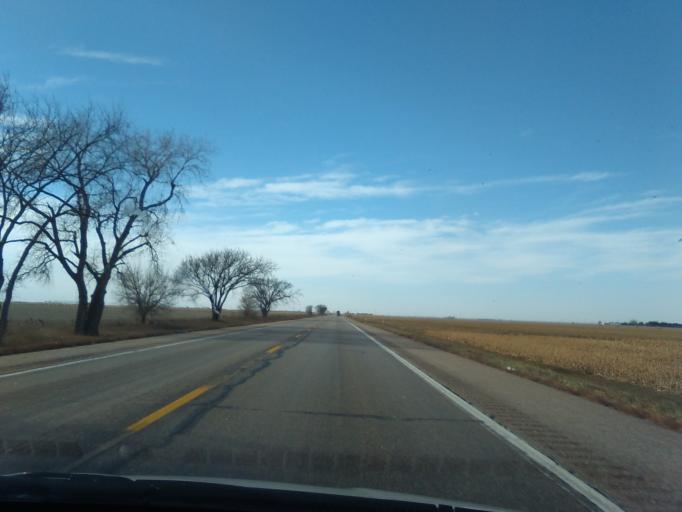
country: US
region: Nebraska
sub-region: Clay County
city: Harvard
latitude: 40.5828
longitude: -98.0912
